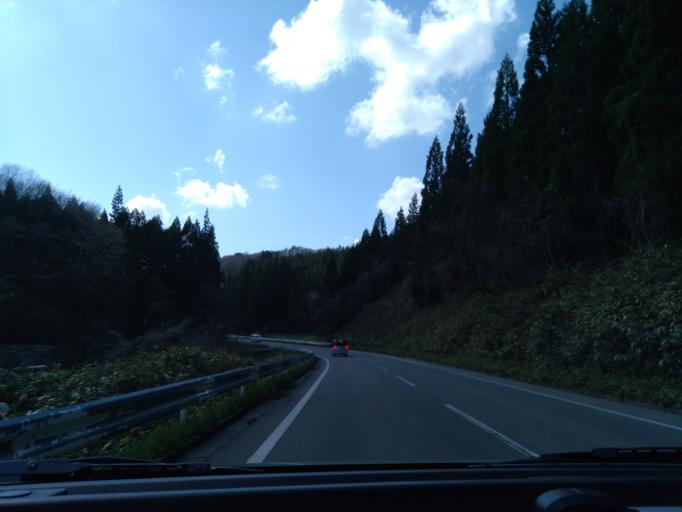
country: JP
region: Akita
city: Akita
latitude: 39.6953
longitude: 140.2380
